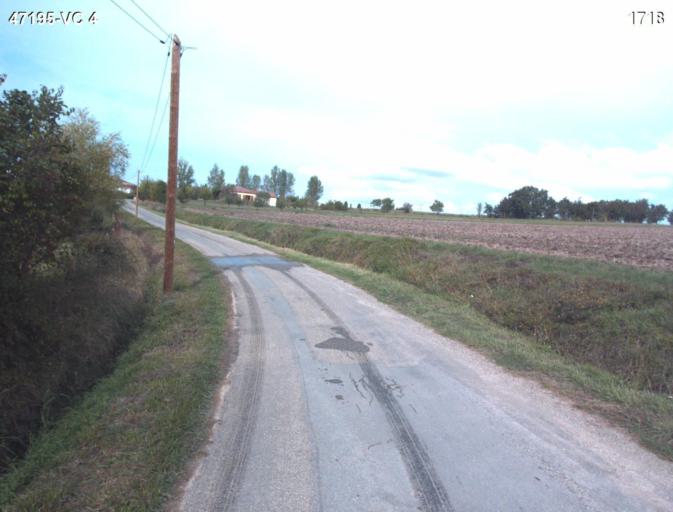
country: FR
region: Aquitaine
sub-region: Departement du Lot-et-Garonne
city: Nerac
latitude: 44.1078
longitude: 0.3860
